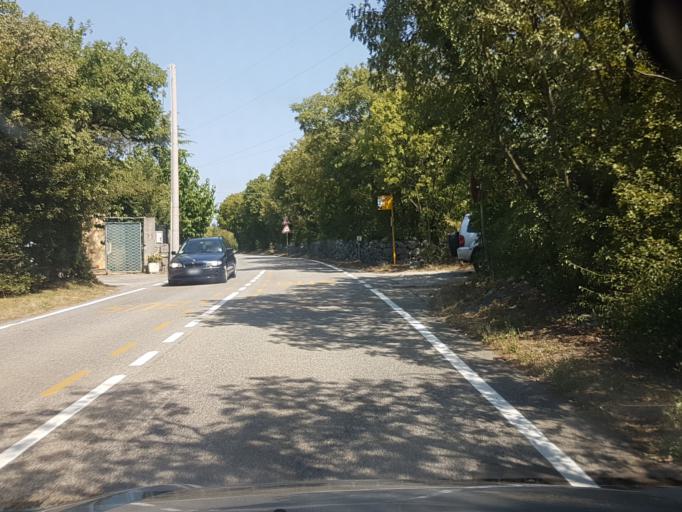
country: IT
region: Friuli Venezia Giulia
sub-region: Provincia di Trieste
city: Aurisina
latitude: 45.7572
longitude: 13.6887
